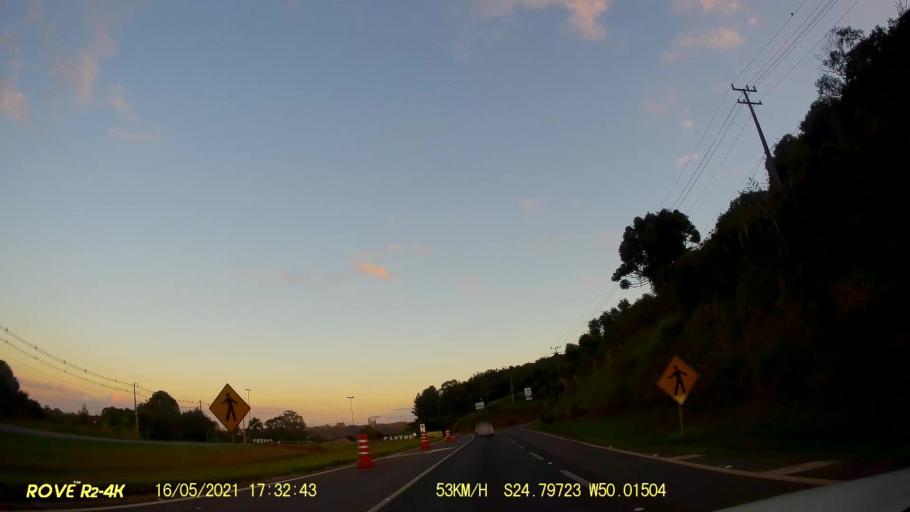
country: BR
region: Parana
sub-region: Castro
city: Castro
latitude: -24.7974
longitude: -50.0150
